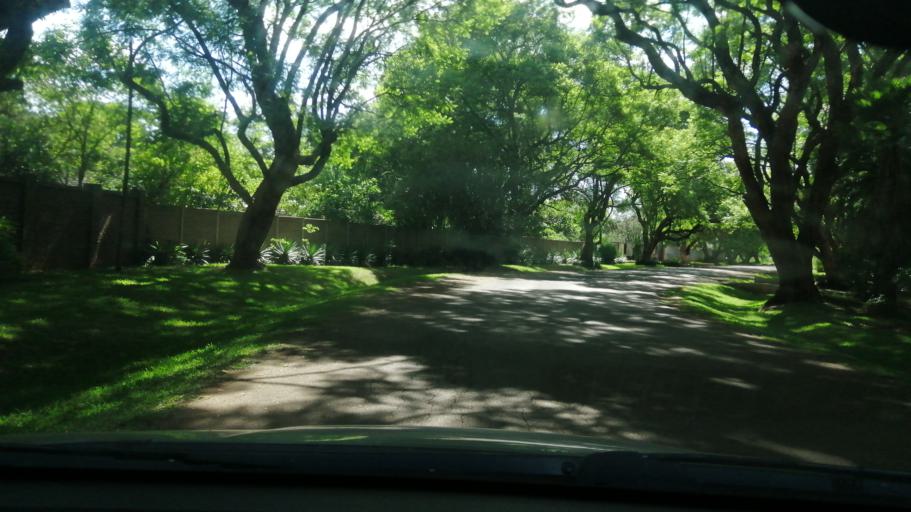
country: ZW
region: Harare
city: Harare
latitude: -17.7558
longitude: 31.0741
